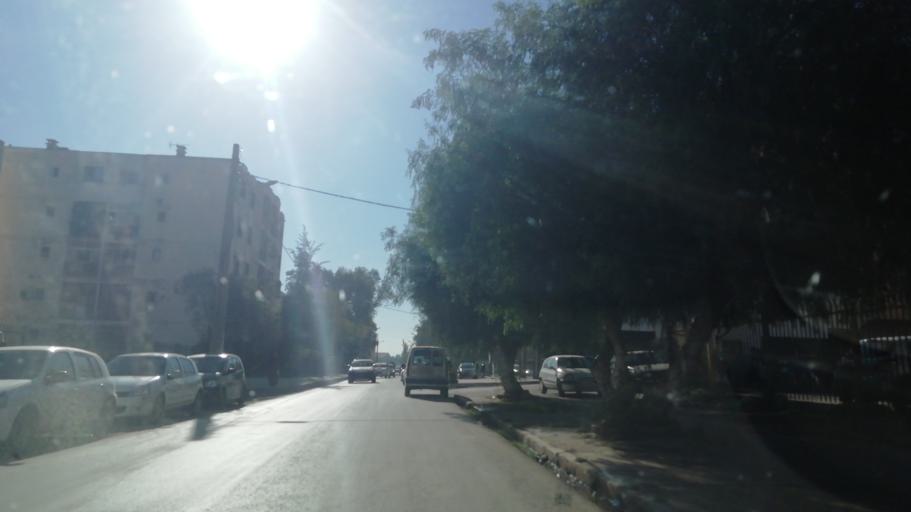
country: DZ
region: Oran
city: Oran
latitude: 35.6701
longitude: -0.6489
